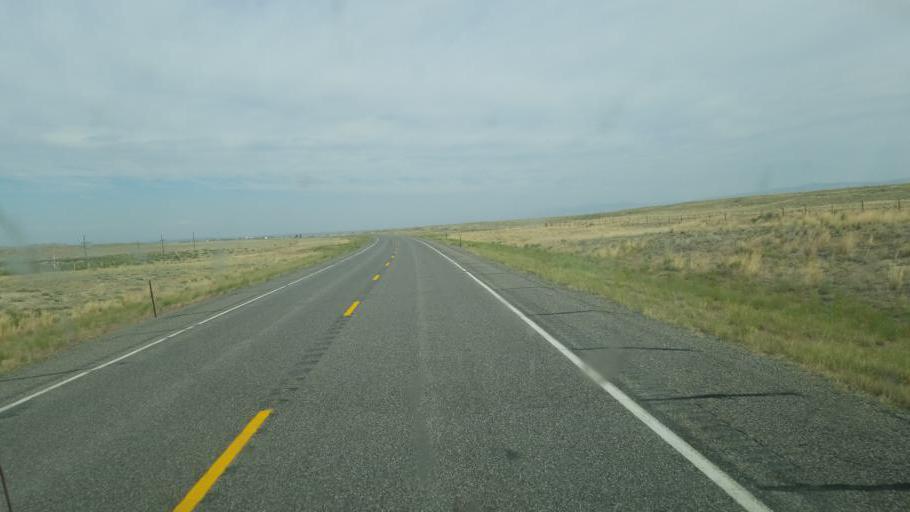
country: US
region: Wyoming
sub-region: Fremont County
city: Riverton
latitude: 43.2341
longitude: -108.0690
